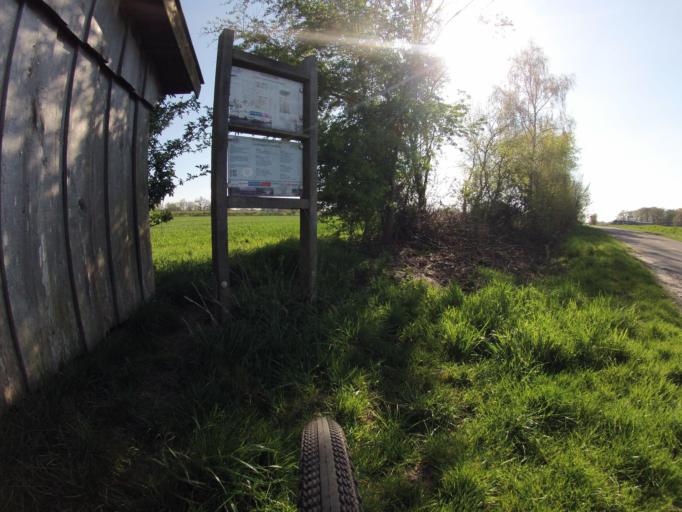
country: DE
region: Lower Saxony
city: Quendorf
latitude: 52.3450
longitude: 7.1786
